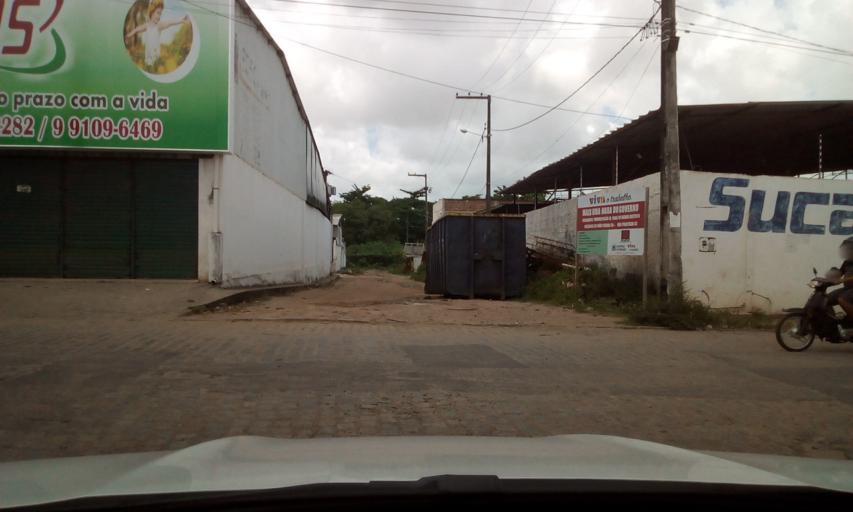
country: BR
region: Paraiba
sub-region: Joao Pessoa
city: Joao Pessoa
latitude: -7.1298
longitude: -34.8879
